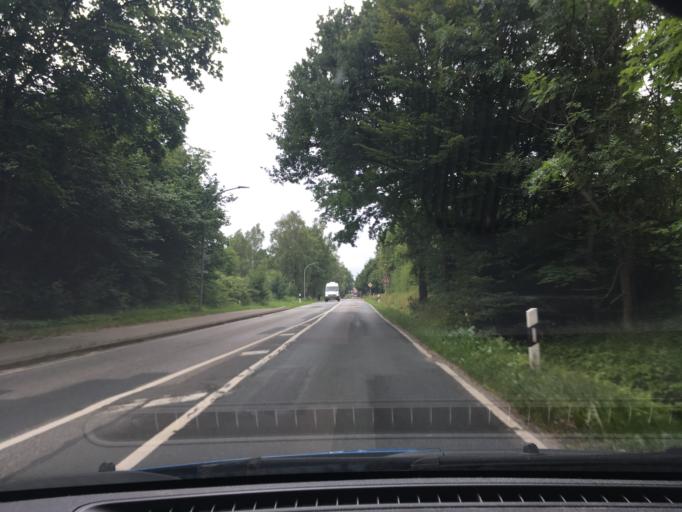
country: DE
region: Lower Saxony
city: Buchholz in der Nordheide
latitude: 53.3760
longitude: 9.9001
